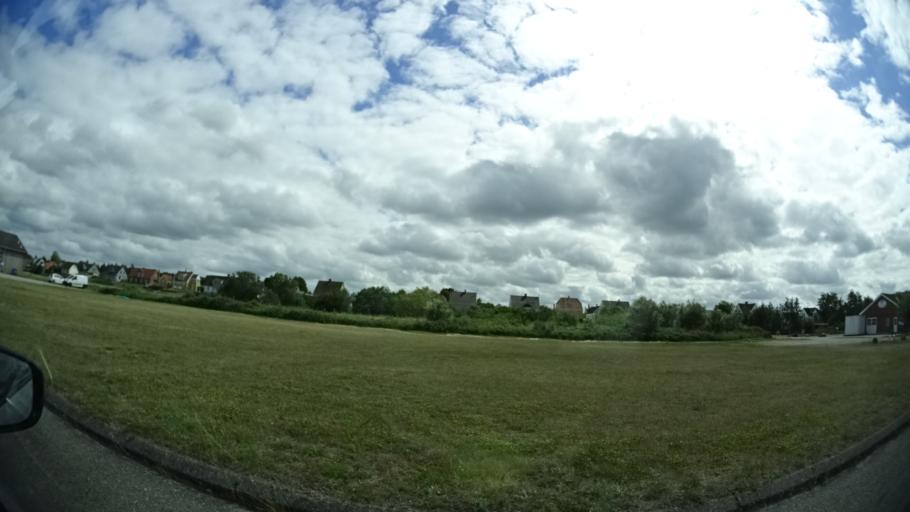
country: DK
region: Central Jutland
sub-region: Norddjurs Kommune
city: Grenaa
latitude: 56.5319
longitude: 10.7146
